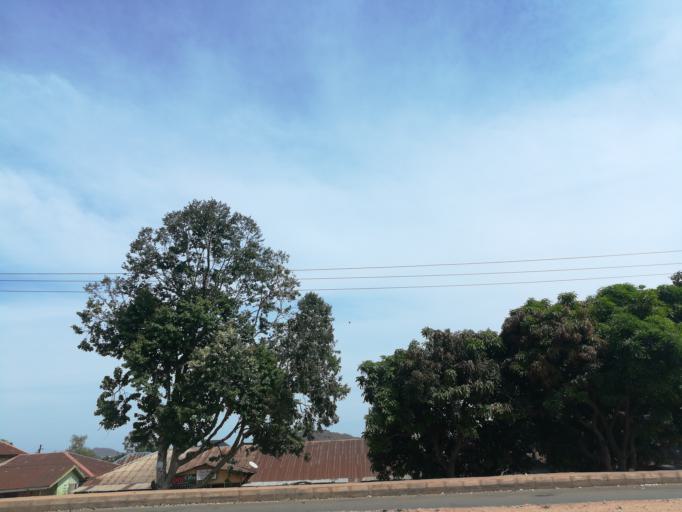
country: NG
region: Plateau
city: Bukuru
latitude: 9.7618
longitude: 8.8596
